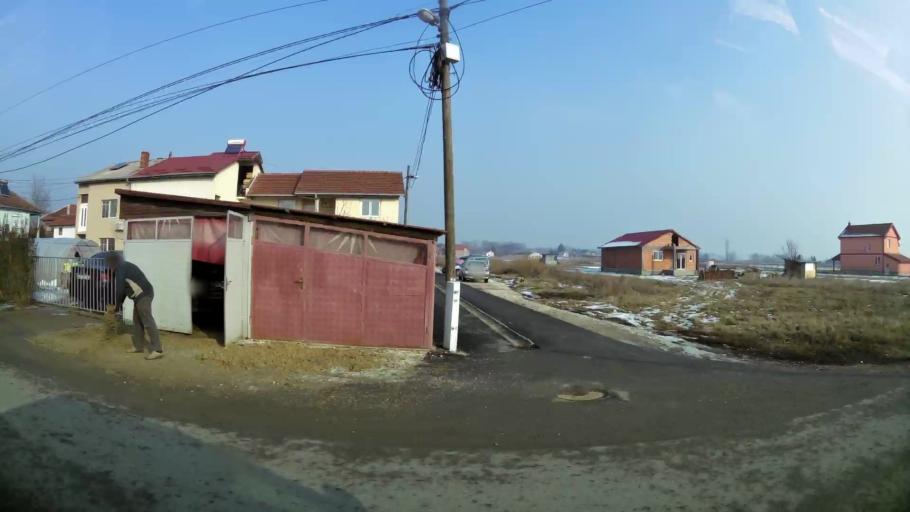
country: MK
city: Kadino
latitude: 41.9788
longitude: 21.5932
